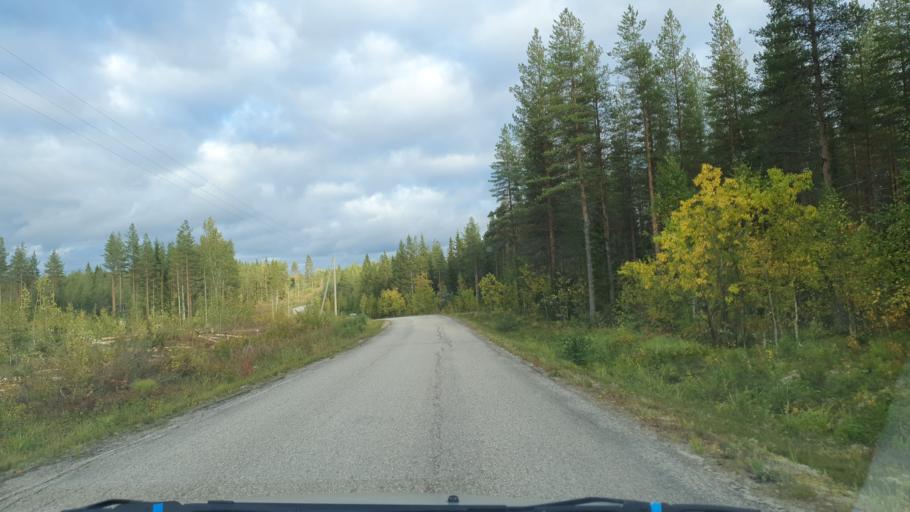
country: FI
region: North Karelia
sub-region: Pielisen Karjala
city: Lieksa
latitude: 63.9209
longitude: 30.1423
